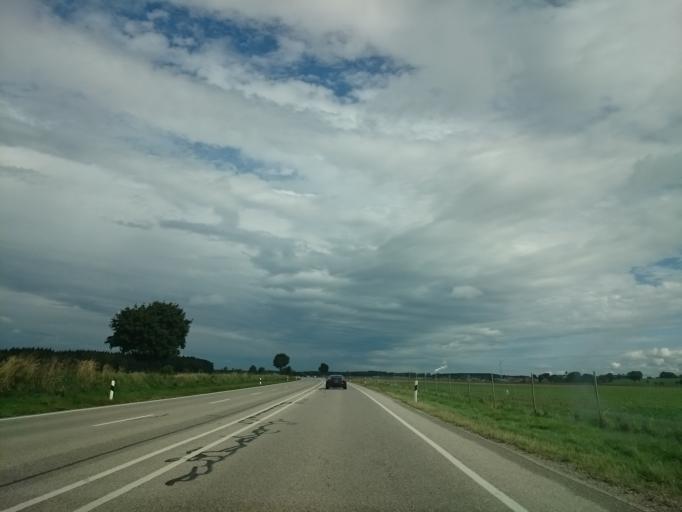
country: DE
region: Bavaria
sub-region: Swabia
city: Rieden
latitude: 47.9539
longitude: 10.6789
